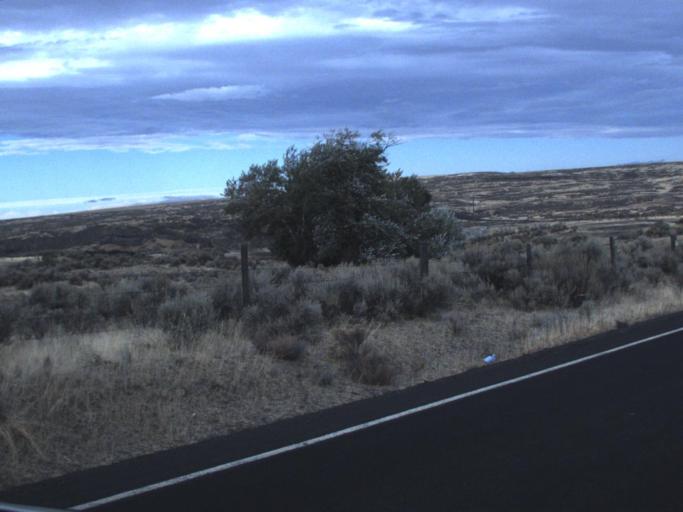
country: US
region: Washington
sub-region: Adams County
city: Ritzville
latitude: 47.4122
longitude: -118.6833
